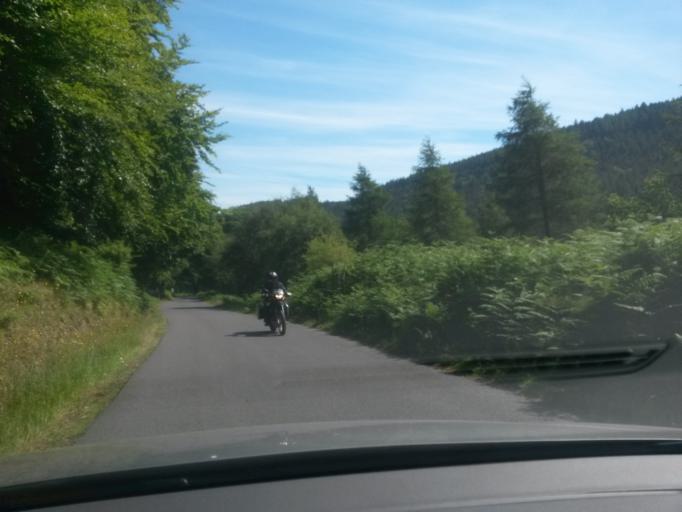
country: IE
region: Leinster
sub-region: Wicklow
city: Enniskerry
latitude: 53.1514
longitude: -6.2018
